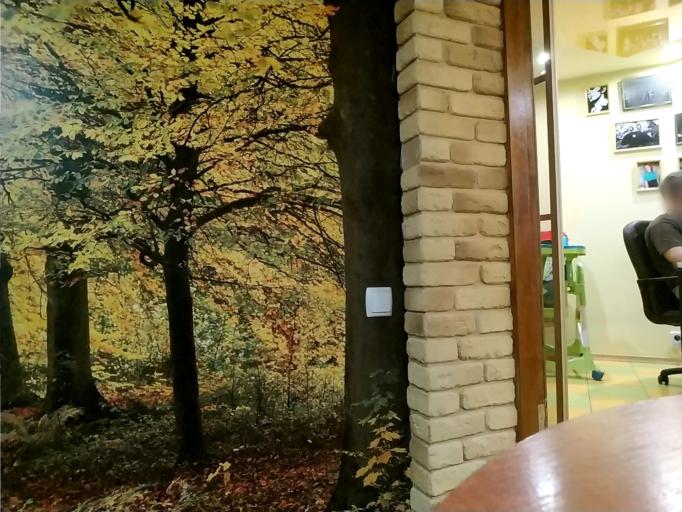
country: RU
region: Tverskaya
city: Zapadnaya Dvina
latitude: 56.3304
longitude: 31.8897
